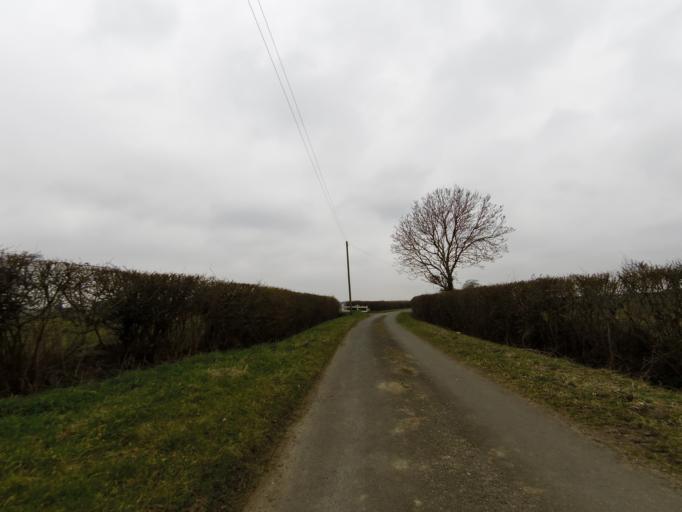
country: GB
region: England
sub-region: Suffolk
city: Cookley
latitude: 52.2620
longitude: 1.4359
